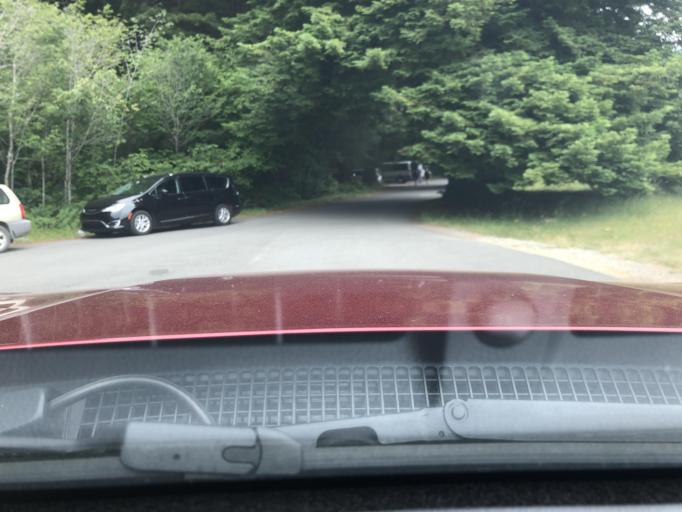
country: US
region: California
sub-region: Humboldt County
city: Westhaven-Moonstone
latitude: 41.3619
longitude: -124.0254
